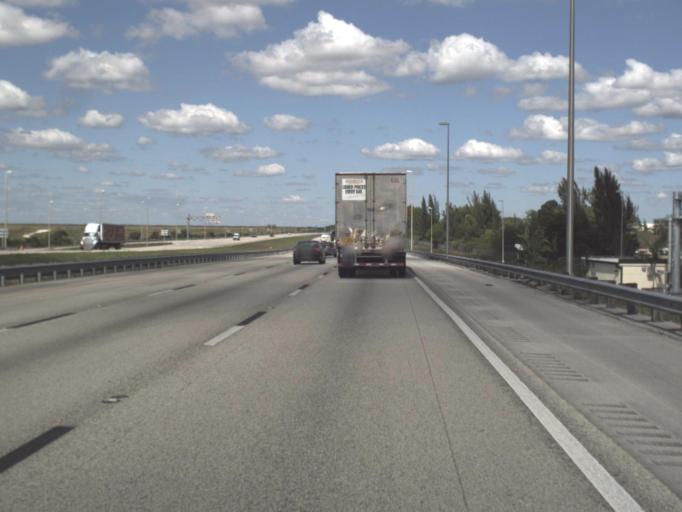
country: US
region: Florida
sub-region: Broward County
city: Coral Springs
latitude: 26.2749
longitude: -80.2965
